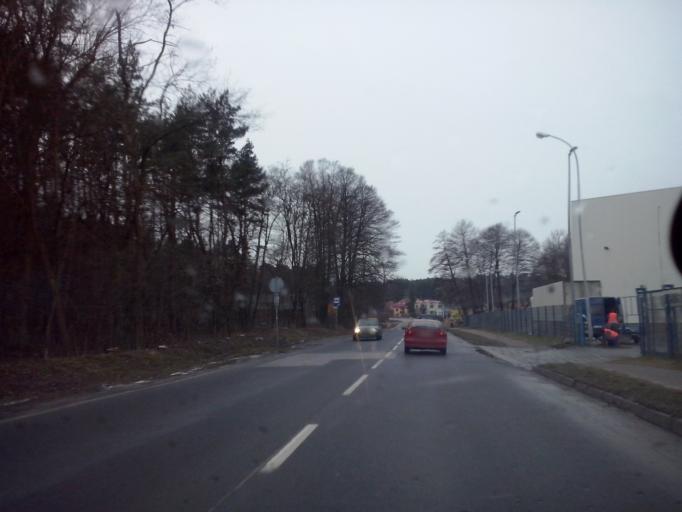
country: PL
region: Lublin Voivodeship
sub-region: Powiat zamojski
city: Zwierzyniec
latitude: 50.6105
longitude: 22.9588
